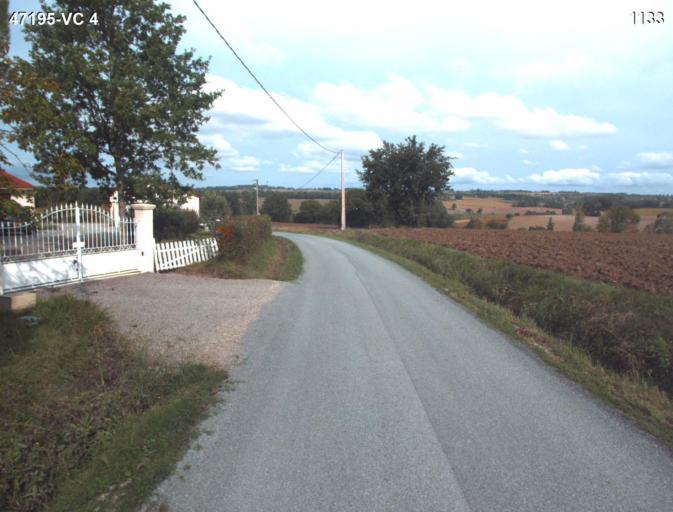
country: FR
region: Aquitaine
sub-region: Departement du Lot-et-Garonne
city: Nerac
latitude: 44.1117
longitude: 0.3819
